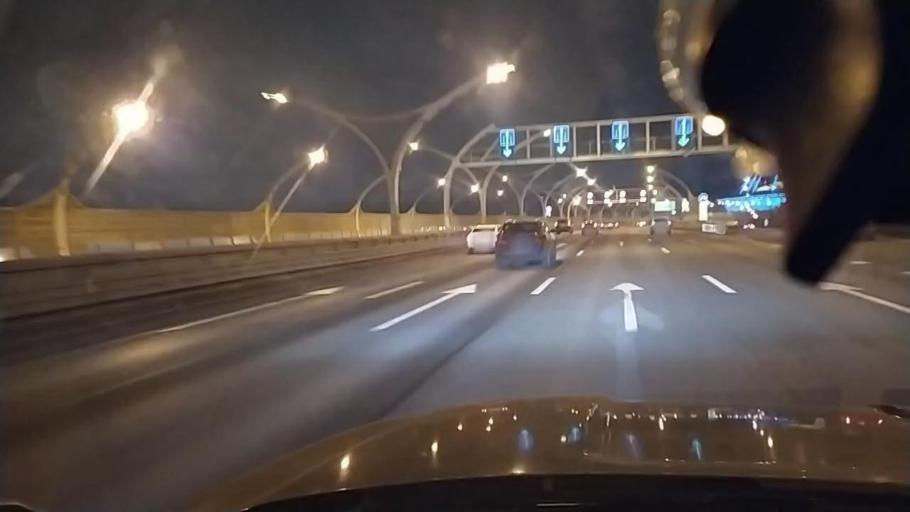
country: RU
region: St.-Petersburg
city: Staraya Derevnya
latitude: 59.9856
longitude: 30.2298
